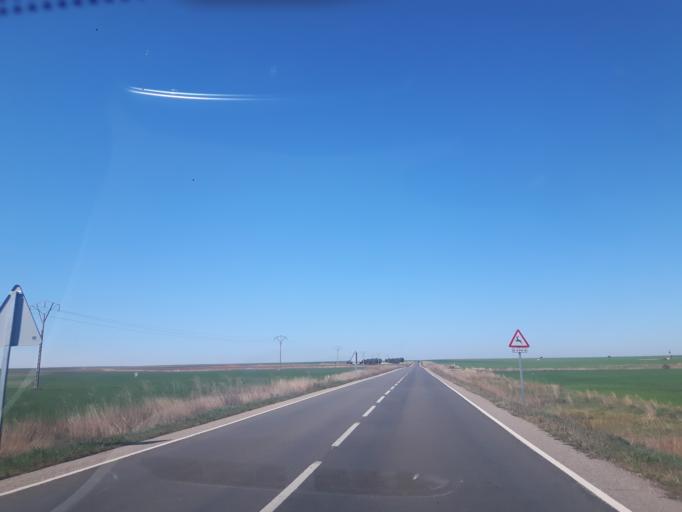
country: ES
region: Castille and Leon
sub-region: Provincia de Salamanca
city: Nava de Sotrobal
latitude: 40.8872
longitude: -5.2911
